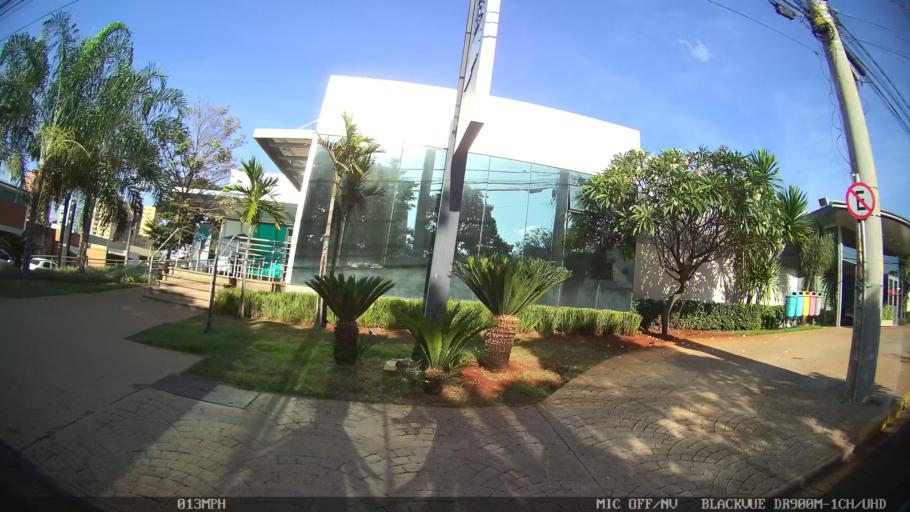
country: BR
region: Sao Paulo
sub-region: Ribeirao Preto
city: Ribeirao Preto
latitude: -21.1881
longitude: -47.8046
